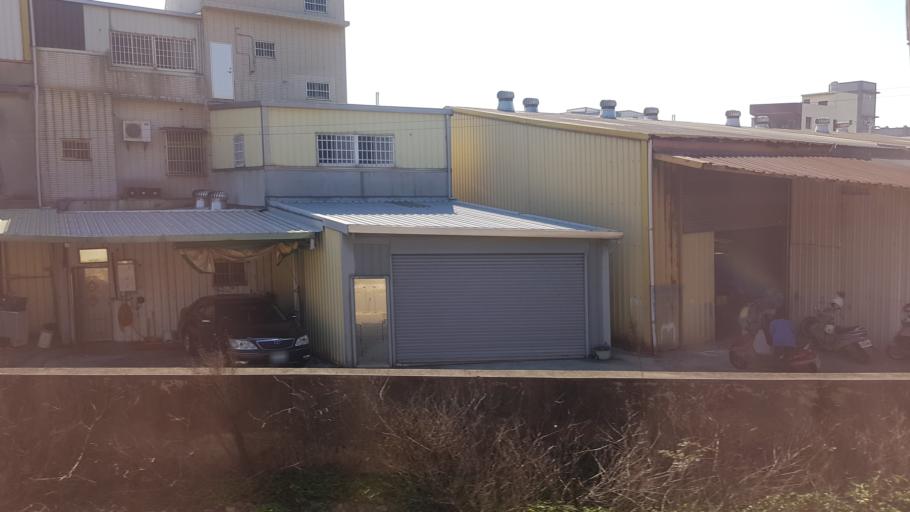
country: TW
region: Taiwan
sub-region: Hsinchu
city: Hsinchu
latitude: 24.6964
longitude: 120.8804
